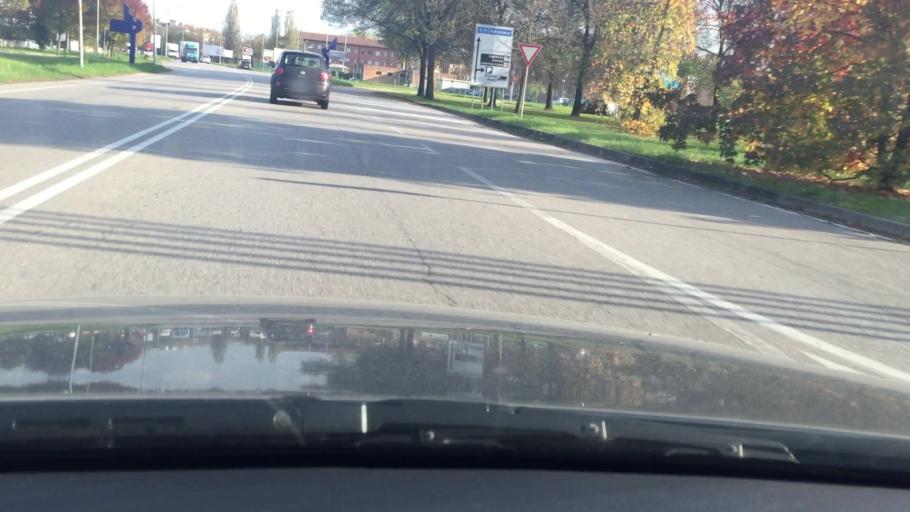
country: IT
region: Emilia-Romagna
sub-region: Provincia di Ferrara
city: Ferrara
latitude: 44.8171
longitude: 11.6083
